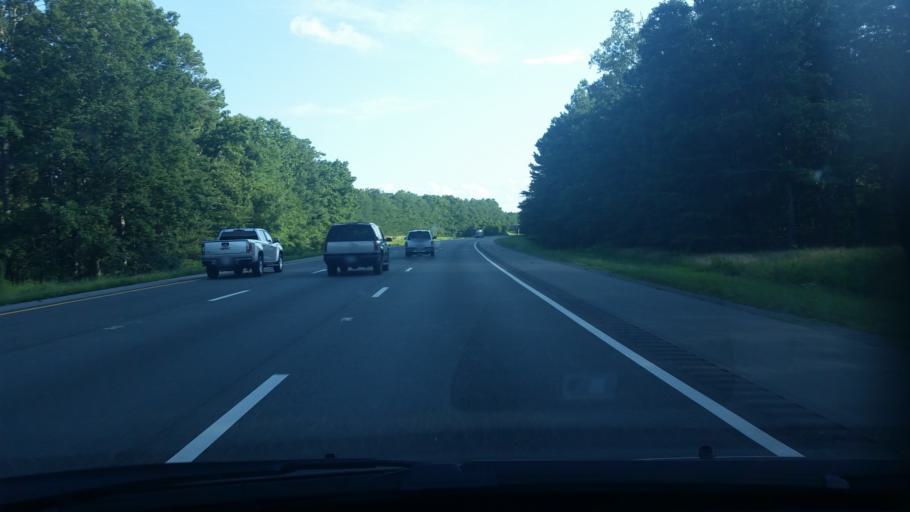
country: US
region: Virginia
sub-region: Henrico County
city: Sandston
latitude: 37.5156
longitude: -77.2721
